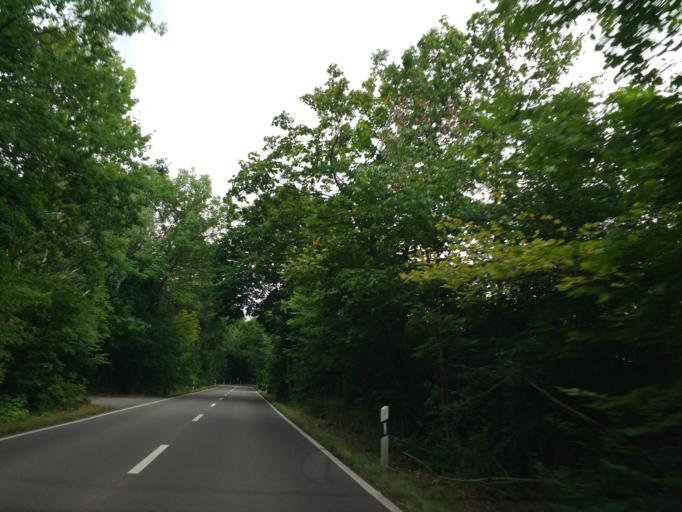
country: DE
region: Saxony-Anhalt
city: Dieskau
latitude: 51.4297
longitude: 12.0281
